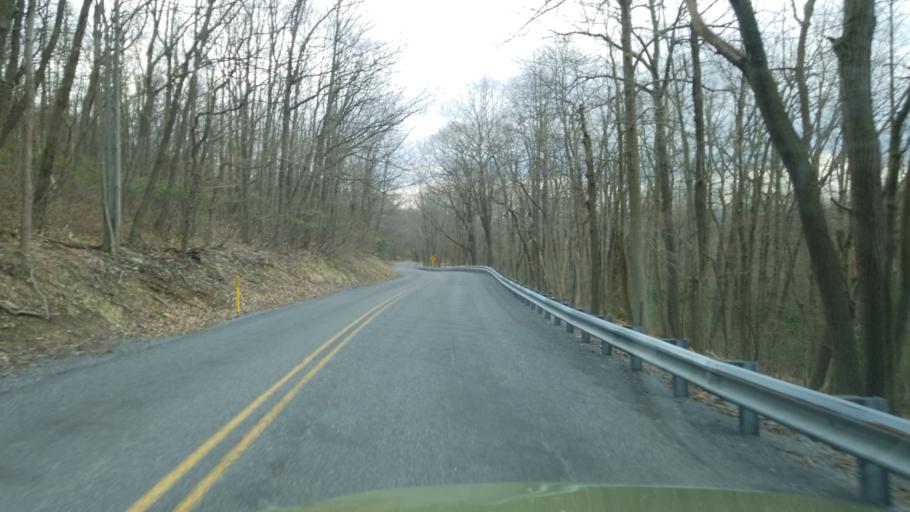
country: US
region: Pennsylvania
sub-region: Blair County
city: Tipton
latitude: 40.7109
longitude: -78.3442
